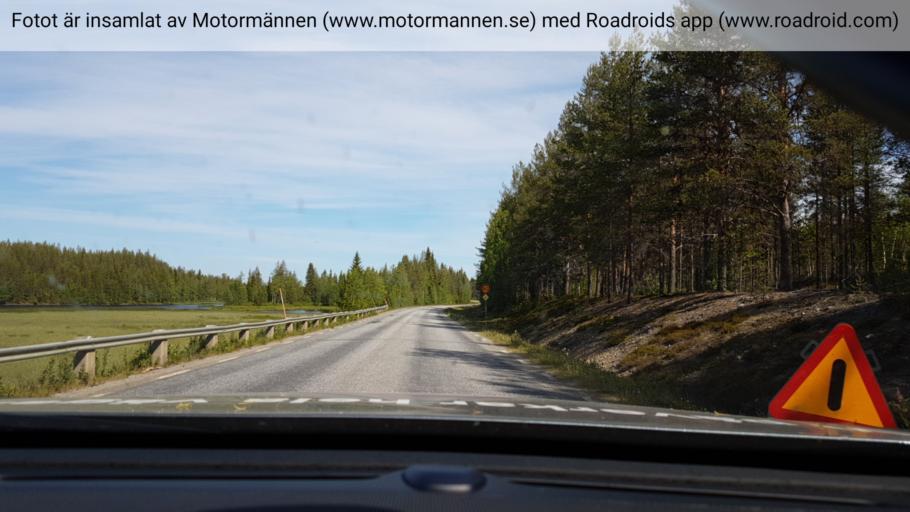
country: SE
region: Vaesterbotten
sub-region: Vilhelmina Kommun
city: Sjoberg
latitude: 64.4682
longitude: 15.9512
